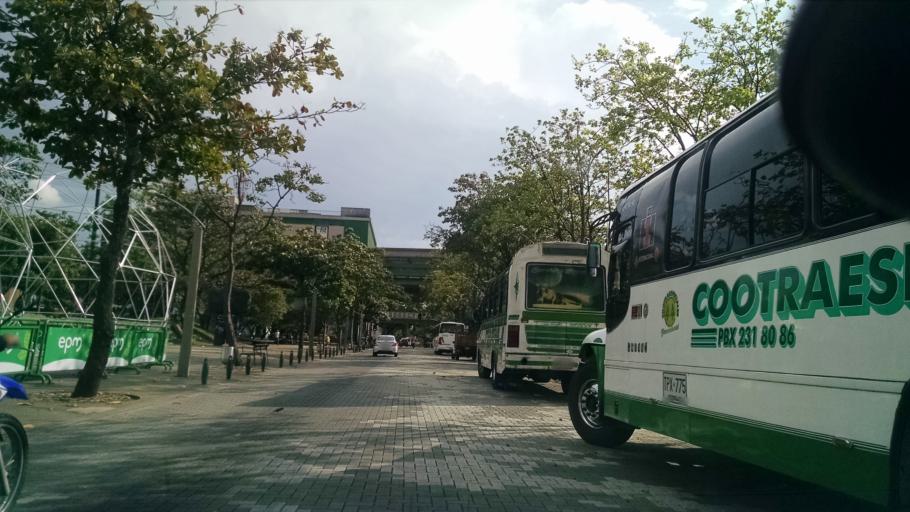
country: CO
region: Antioquia
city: Medellin
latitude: 6.2705
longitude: -75.5653
